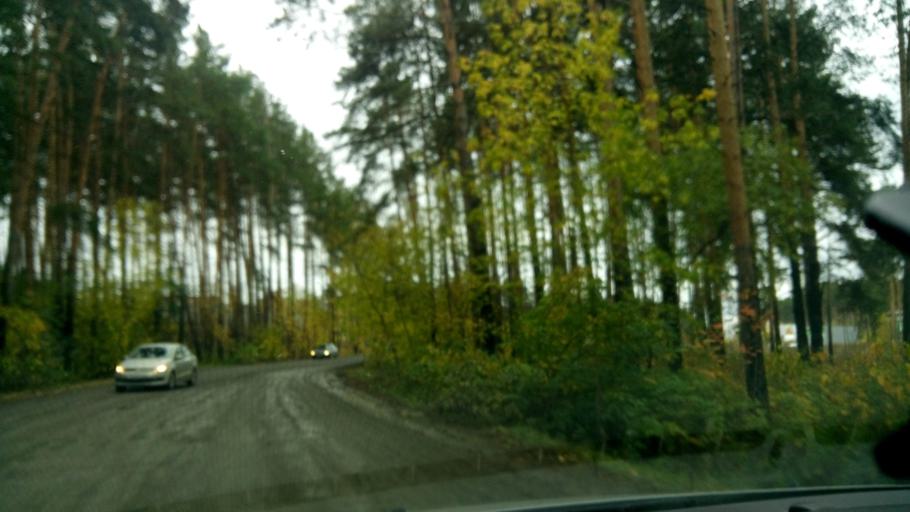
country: RU
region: Sverdlovsk
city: Shirokaya Rechka
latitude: 56.8178
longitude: 60.5232
